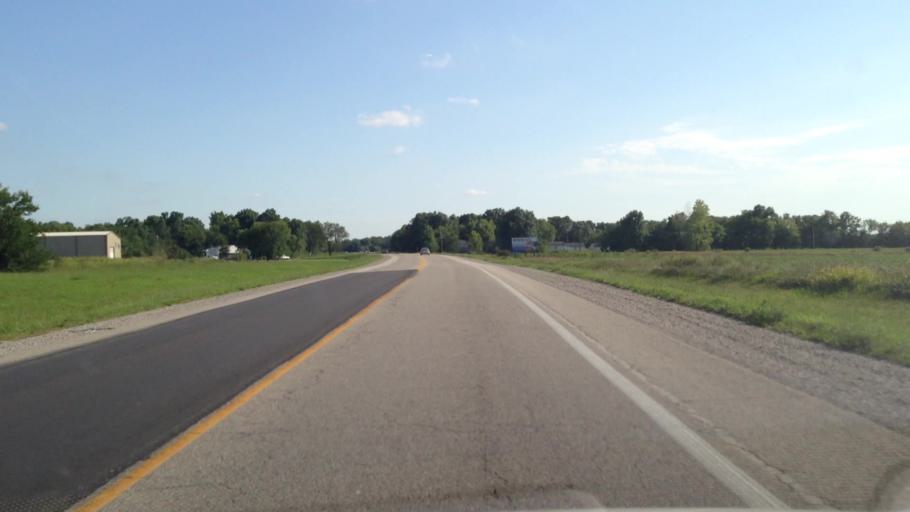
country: US
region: Kansas
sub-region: Crawford County
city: Arma
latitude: 37.5318
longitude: -94.7110
